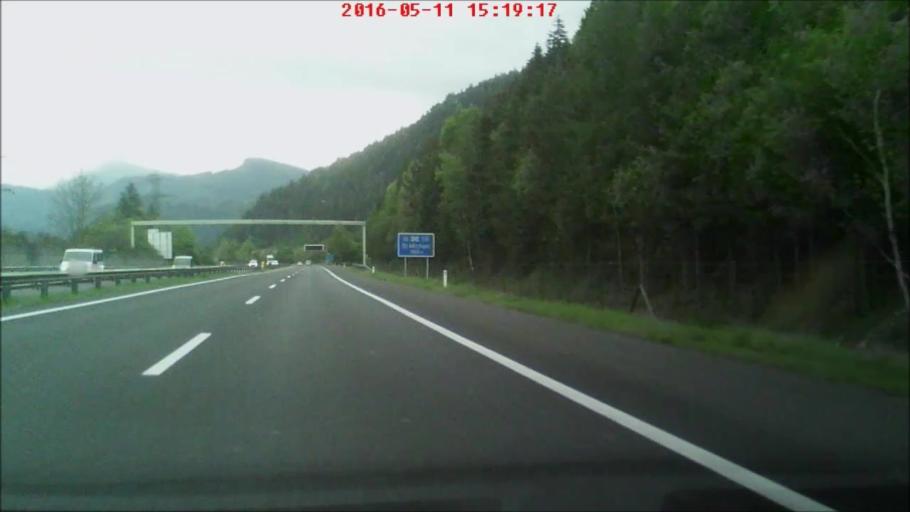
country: AT
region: Styria
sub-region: Politischer Bezirk Leoben
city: Traboch
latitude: 47.3616
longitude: 14.9993
